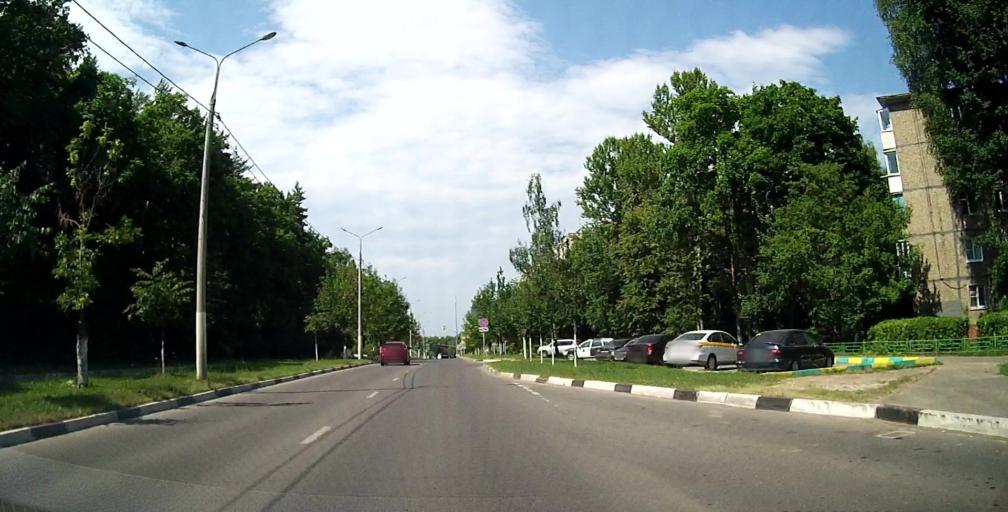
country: RU
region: Moskovskaya
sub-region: Podol'skiy Rayon
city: Podol'sk
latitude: 55.4159
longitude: 37.5212
